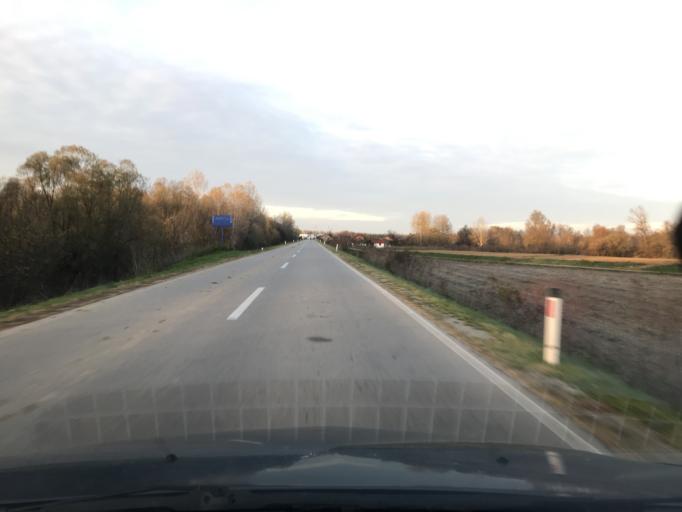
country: HR
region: Sisacko-Moslavacka
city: Novska
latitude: 45.2573
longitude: 16.9157
